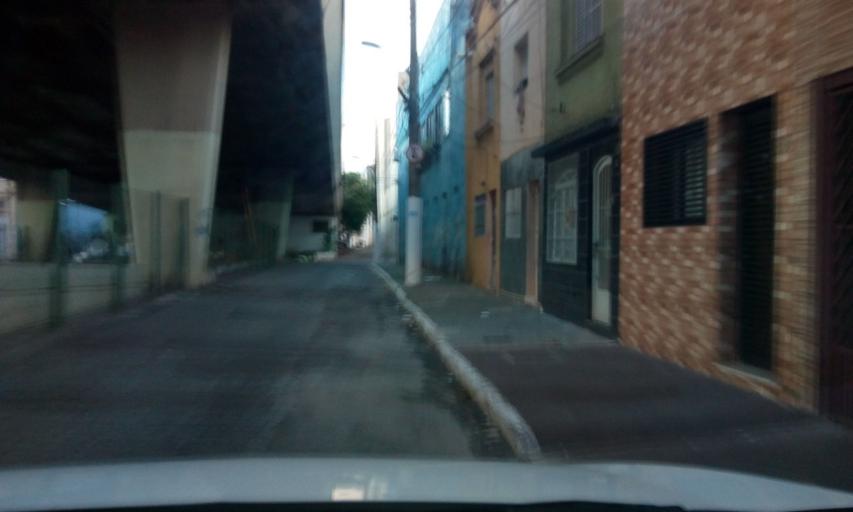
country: BR
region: Sao Paulo
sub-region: Sao Paulo
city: Sao Paulo
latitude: -23.5430
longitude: -46.5939
